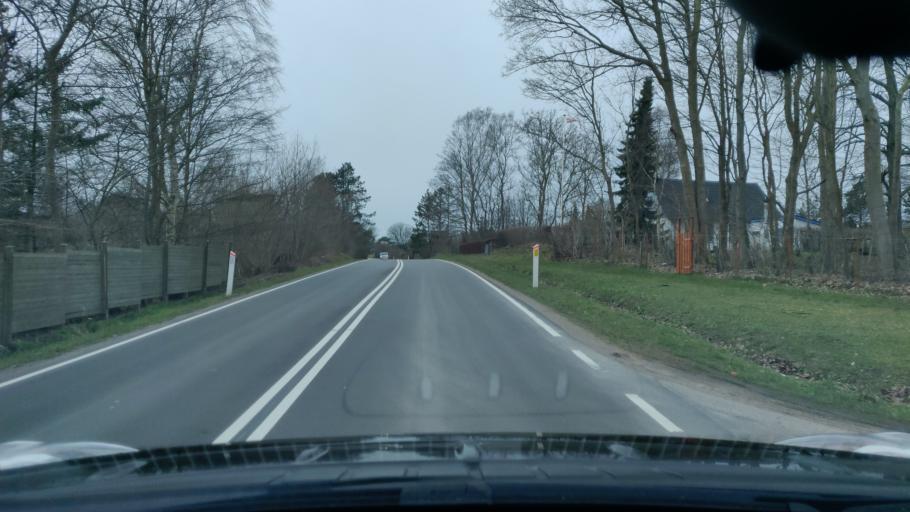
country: DK
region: Zealand
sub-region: Odsherred Kommune
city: Hojby
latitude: 55.9308
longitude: 11.6143
